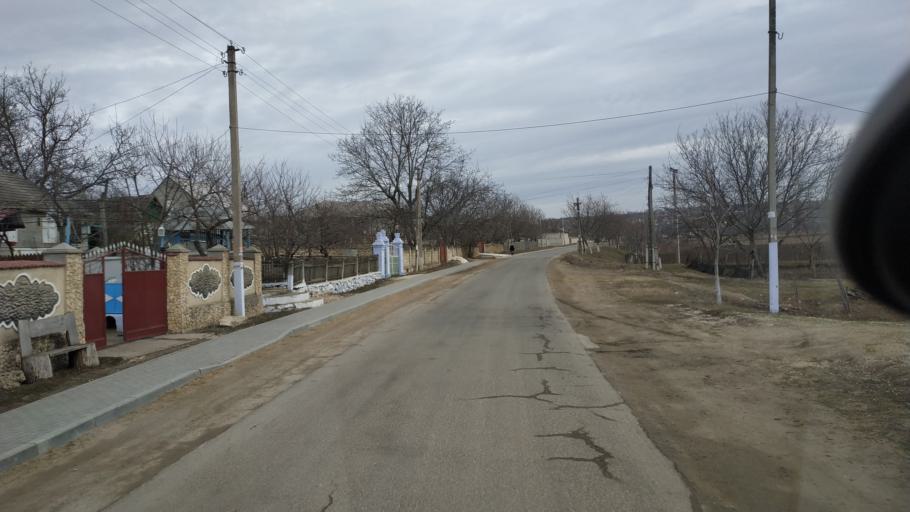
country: MD
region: Telenesti
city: Cocieri
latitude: 47.2655
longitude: 29.0489
